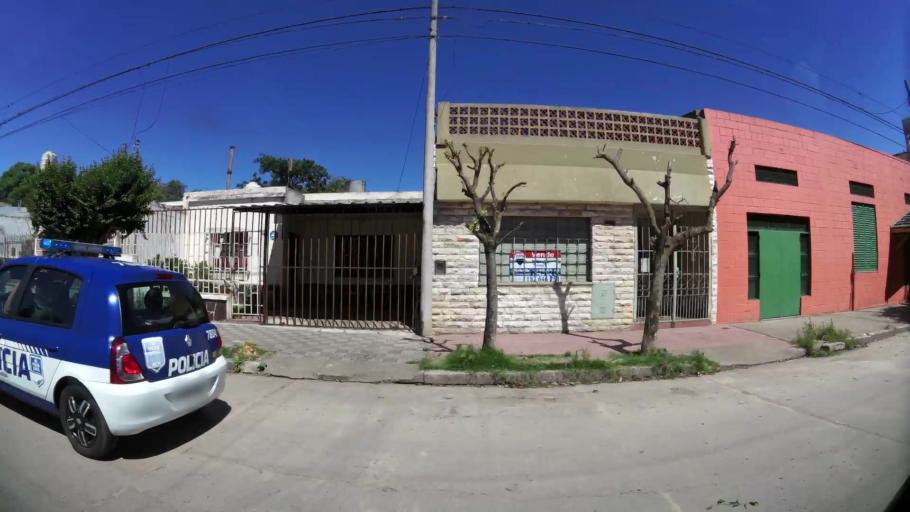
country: AR
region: Cordoba
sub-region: Departamento de Capital
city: Cordoba
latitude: -31.4202
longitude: -64.1374
